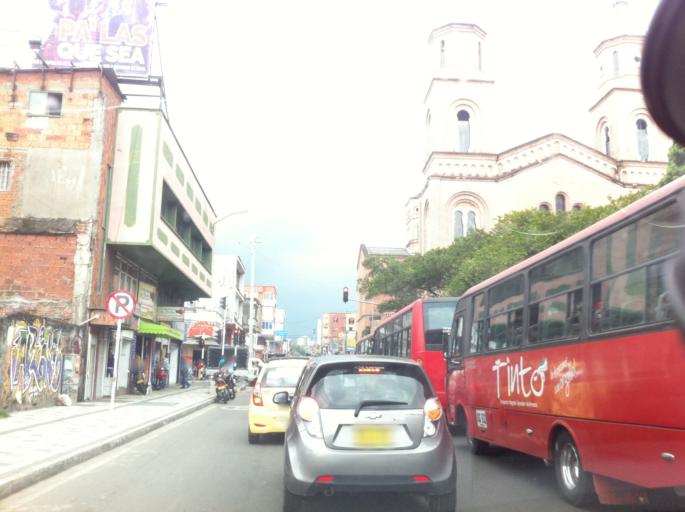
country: CO
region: Quindio
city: Armenia
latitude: 4.5369
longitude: -75.6726
